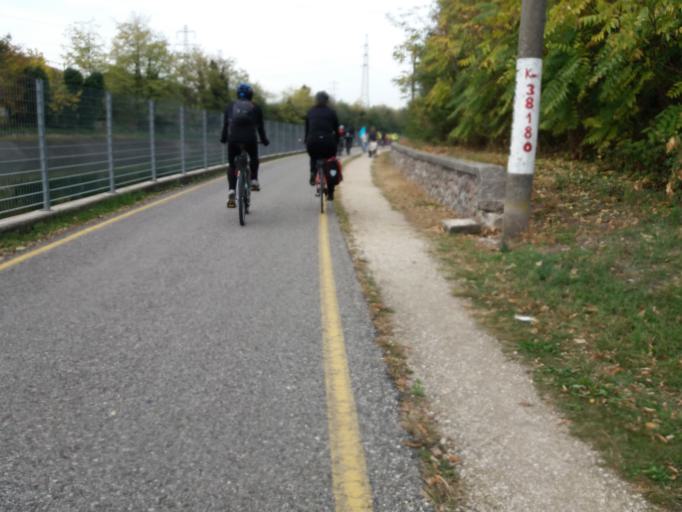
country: IT
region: Veneto
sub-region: Provincia di Verona
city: Bussolengo
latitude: 45.4776
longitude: 10.8358
